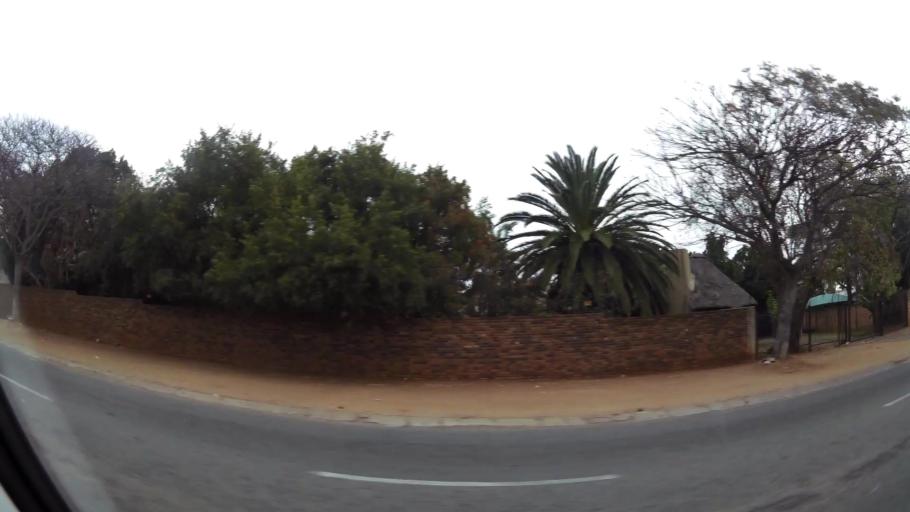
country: ZA
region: Limpopo
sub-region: Capricorn District Municipality
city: Polokwane
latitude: -23.9004
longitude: 29.4714
